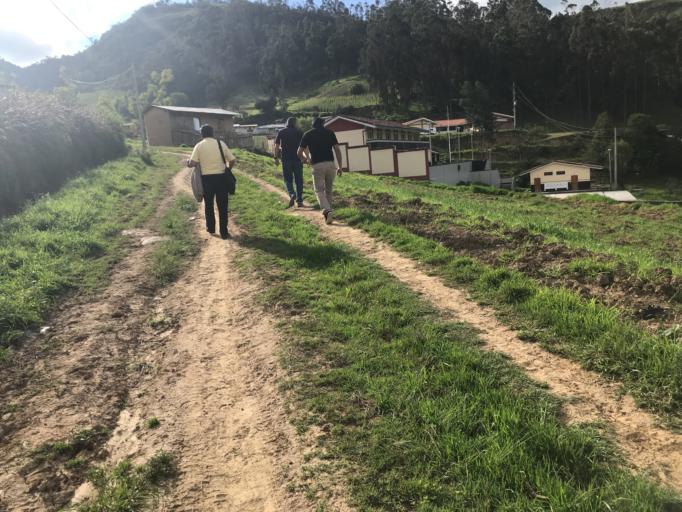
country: PE
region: Cajamarca
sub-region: Provincia de Chota
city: Querocoto
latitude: -6.3576
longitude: -79.0341
